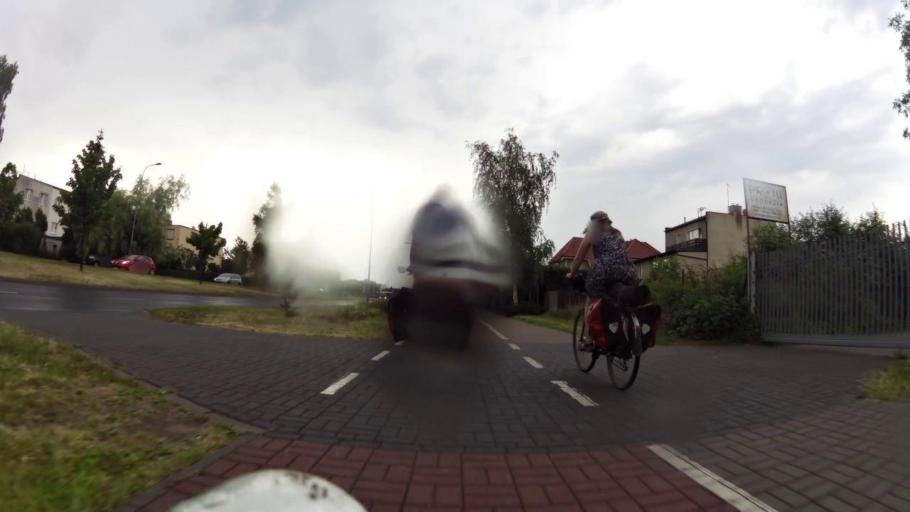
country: PL
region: Kujawsko-Pomorskie
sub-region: Bydgoszcz
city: Bydgoszcz
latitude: 53.1442
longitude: 17.9629
